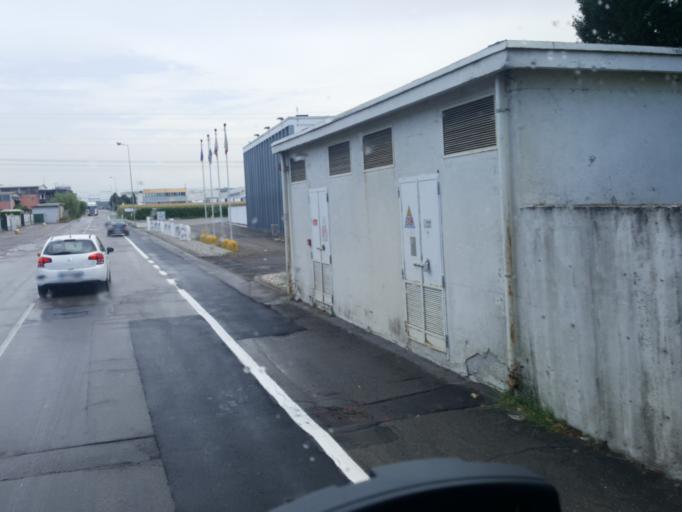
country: IT
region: Lombardy
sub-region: Provincia di Como
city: Turate
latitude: 45.6602
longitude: 9.0180
